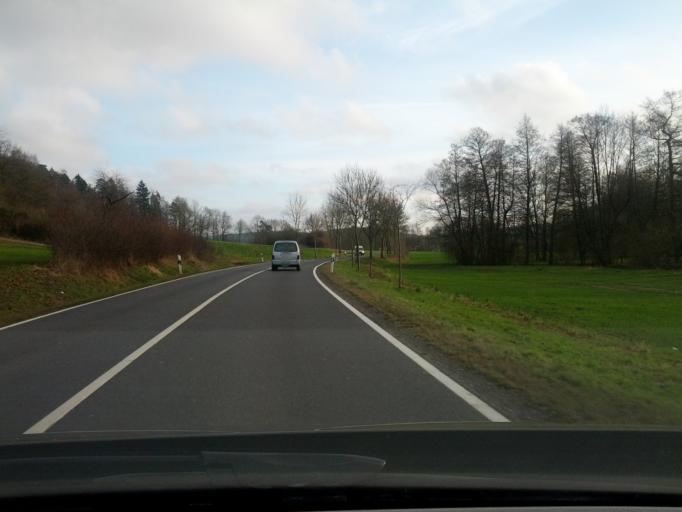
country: DE
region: Thuringia
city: Krauthausen
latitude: 51.0310
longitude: 10.2546
